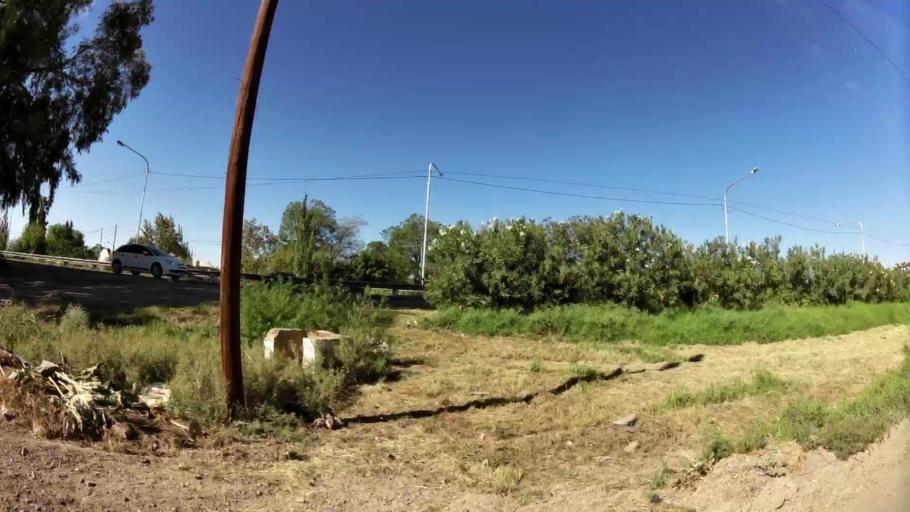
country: AR
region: Mendoza
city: Las Heras
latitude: -32.8366
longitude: -68.8058
